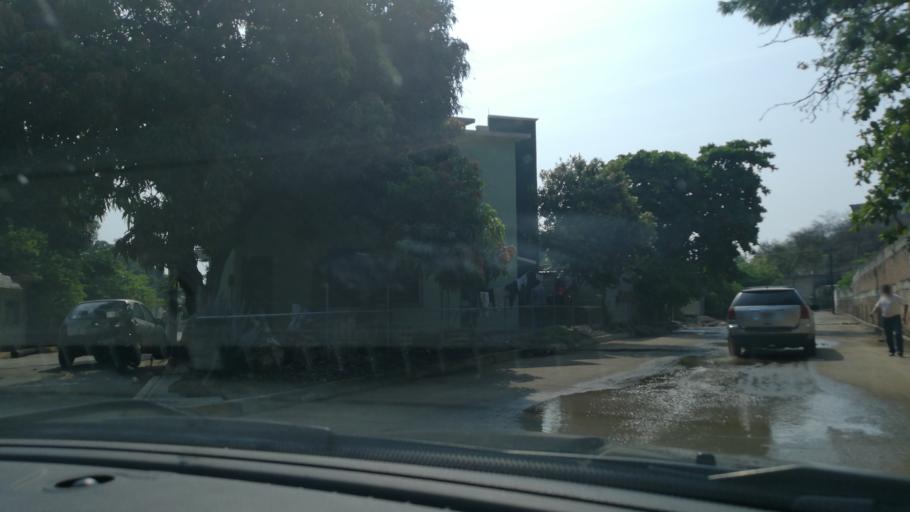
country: MX
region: Oaxaca
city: San Blas Atempa
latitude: 16.3395
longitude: -95.2228
